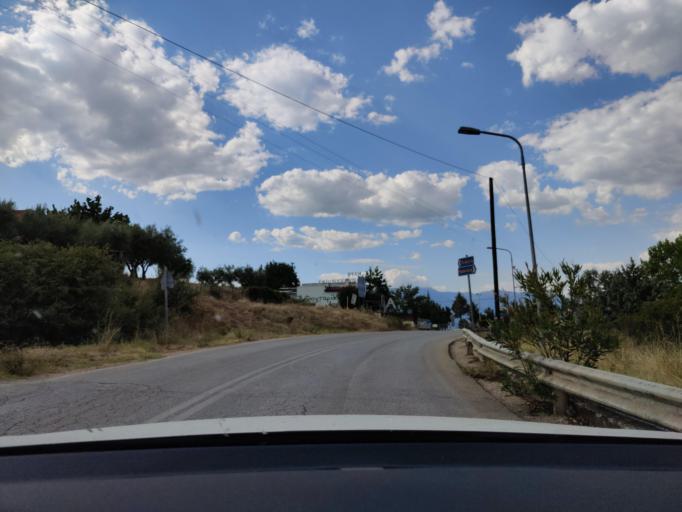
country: GR
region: Central Macedonia
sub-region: Nomos Serron
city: Chrysochorafa
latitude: 41.1370
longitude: 23.2202
